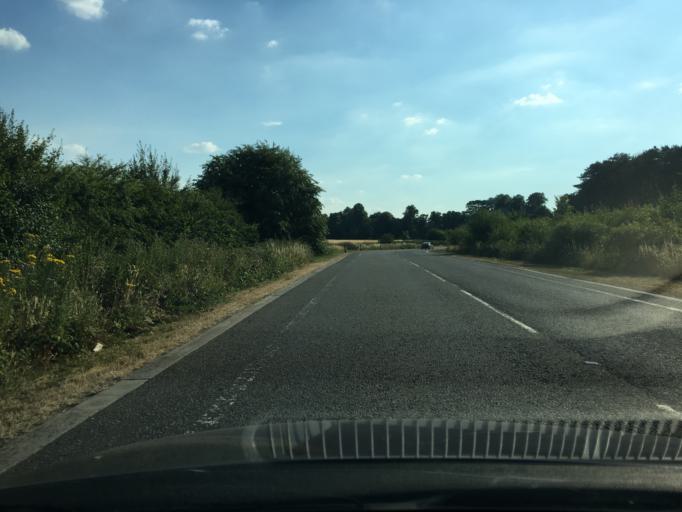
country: GB
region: England
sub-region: Bracknell Forest
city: Binfield
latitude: 51.4062
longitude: -0.7898
